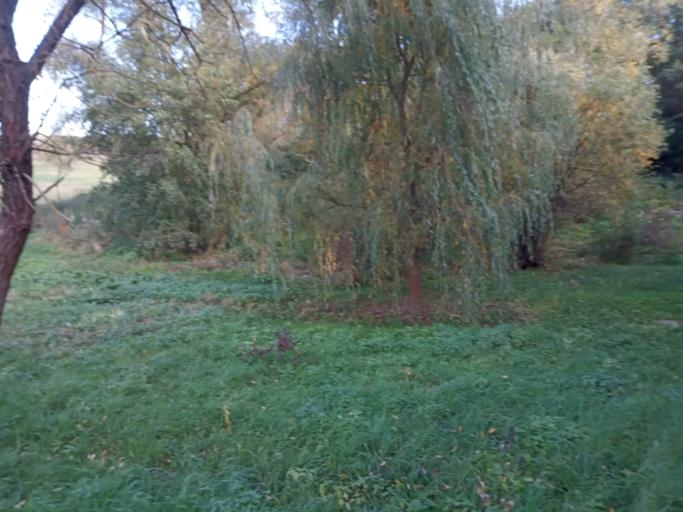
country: HU
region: Nograd
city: Batonyterenye
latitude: 47.9886
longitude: 19.8468
